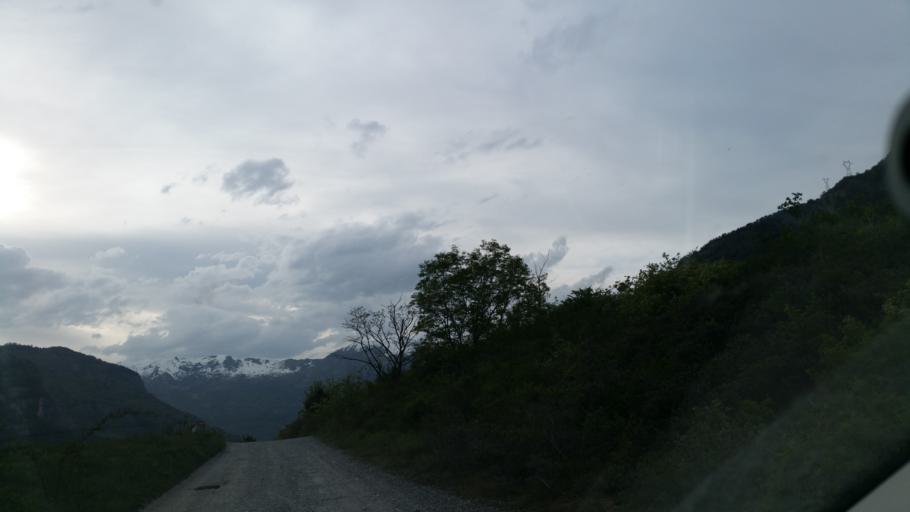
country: FR
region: Rhone-Alpes
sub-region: Departement de la Savoie
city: Villargondran
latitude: 45.2487
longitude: 6.4211
